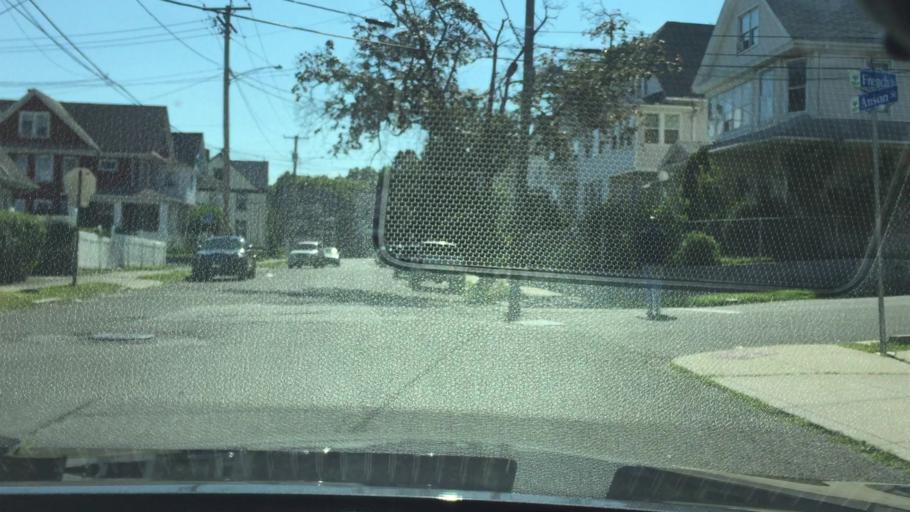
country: US
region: Connecticut
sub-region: Fairfield County
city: Bridgeport
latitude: 41.1983
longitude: -73.1996
